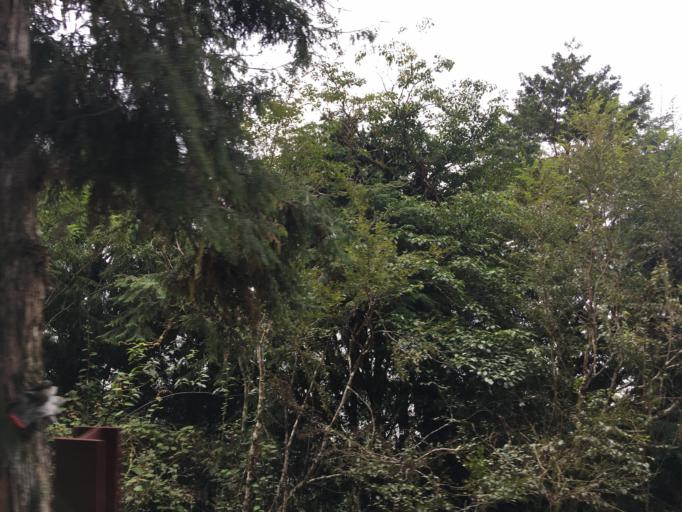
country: TW
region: Taiwan
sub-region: Yilan
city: Yilan
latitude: 24.4891
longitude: 121.5342
